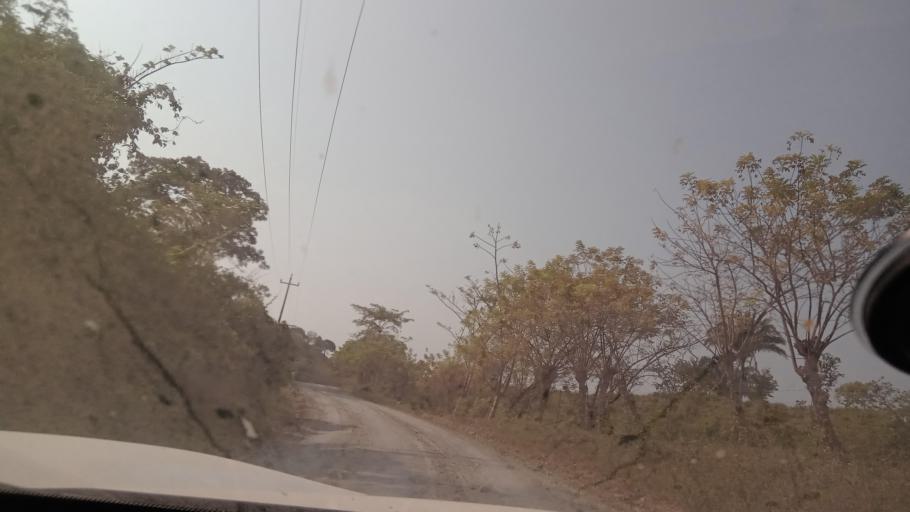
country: MX
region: Tabasco
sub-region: Huimanguillo
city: Francisco Rueda
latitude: 17.6150
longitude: -93.9392
